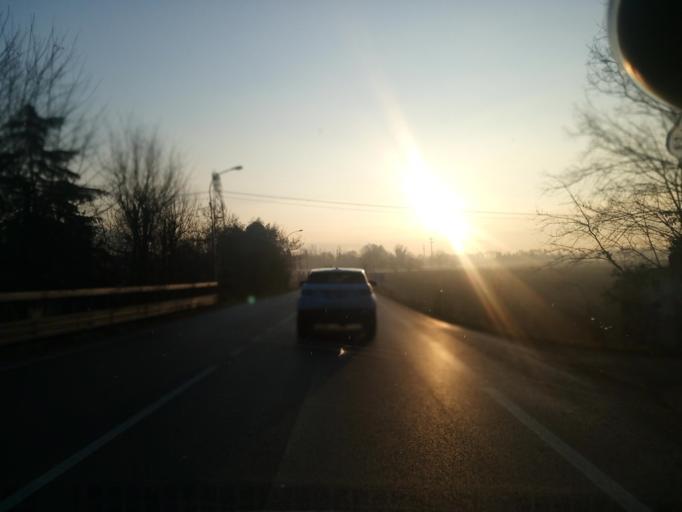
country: IT
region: Veneto
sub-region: Provincia di Vicenza
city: Tezze
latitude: 45.5116
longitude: 11.3777
